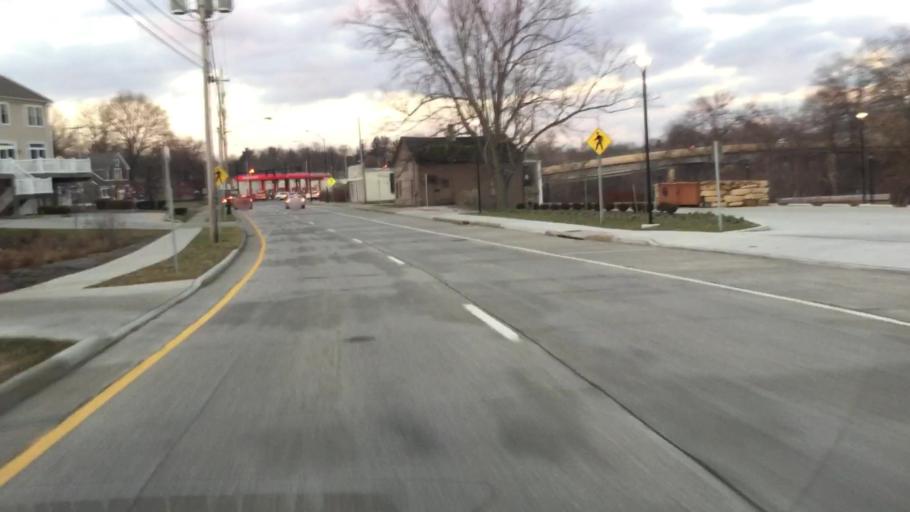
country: US
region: Ohio
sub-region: Portage County
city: Kent
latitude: 41.1568
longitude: -81.3601
